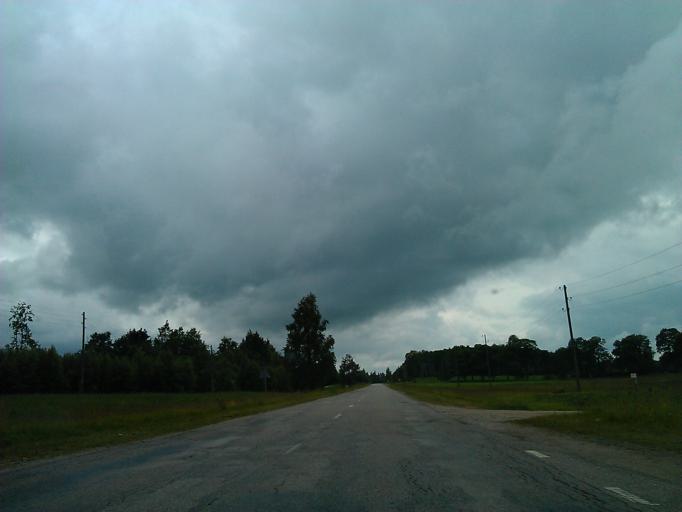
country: LV
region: Kuldigas Rajons
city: Kuldiga
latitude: 56.8583
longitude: 21.8195
